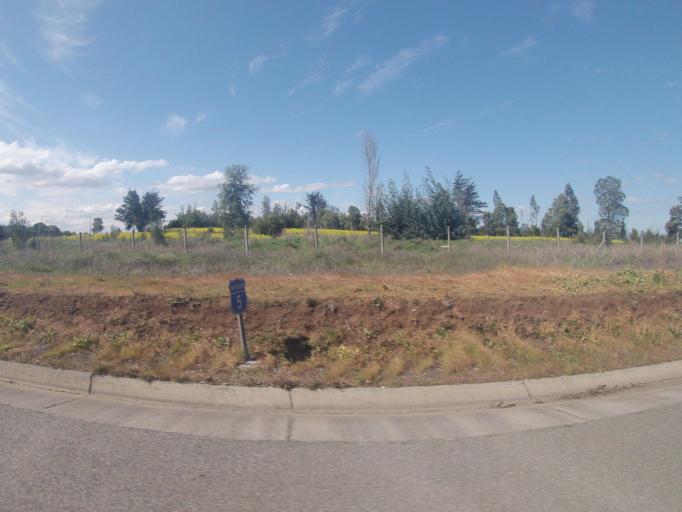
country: CL
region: Biobio
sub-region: Provincia de Biobio
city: Los Angeles
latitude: -37.4470
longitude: -72.4047
